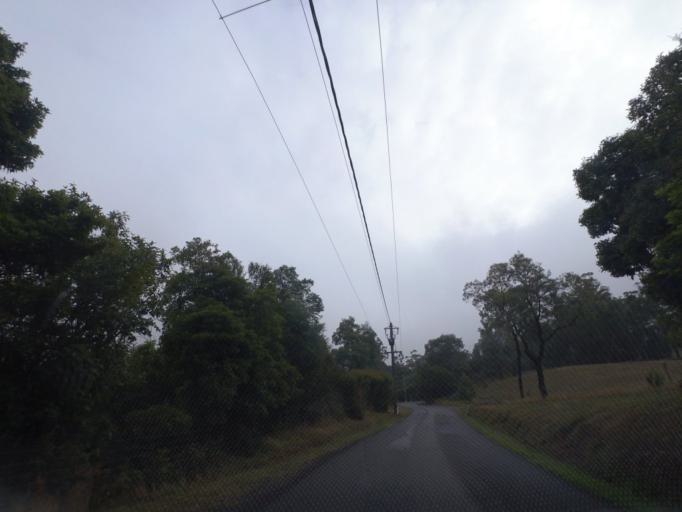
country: AU
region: Victoria
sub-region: Yarra Ranges
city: Launching Place
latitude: -37.7318
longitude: 145.5926
